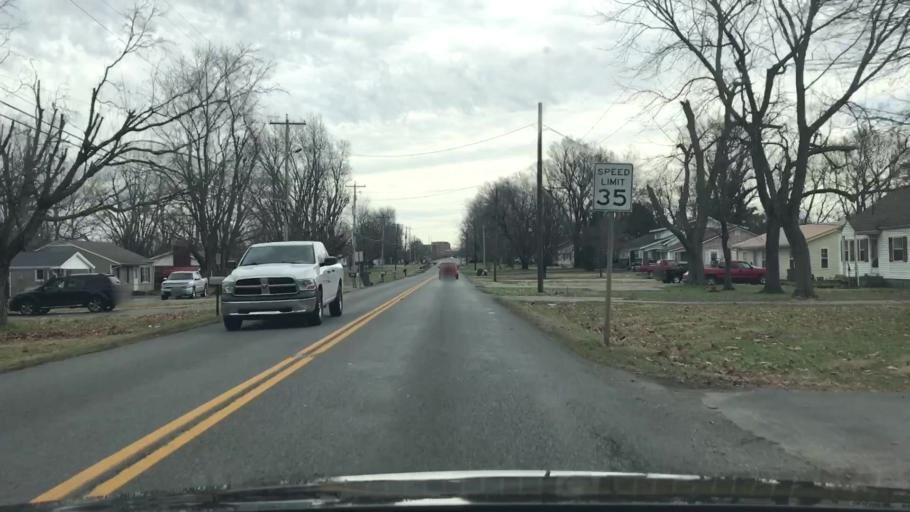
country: US
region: Kentucky
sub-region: Christian County
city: Hopkinsville
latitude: 36.8606
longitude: -87.5097
